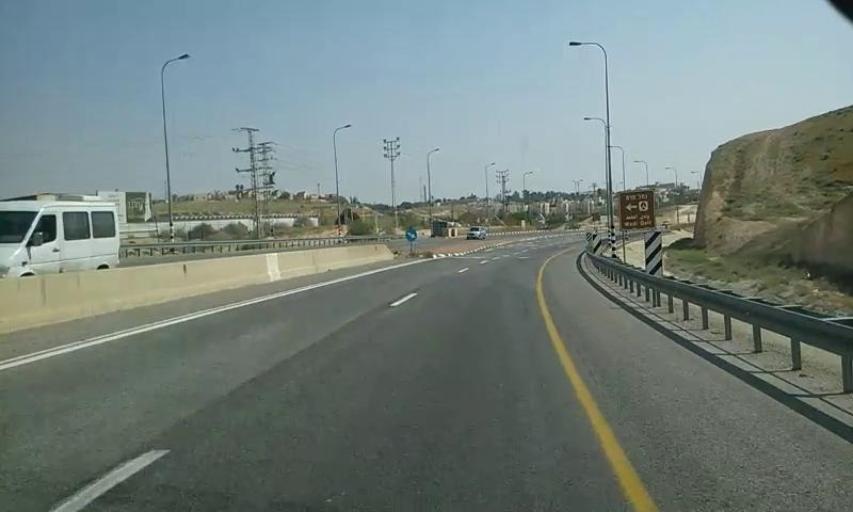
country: PS
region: West Bank
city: Jericho
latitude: 31.8197
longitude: 35.3890
